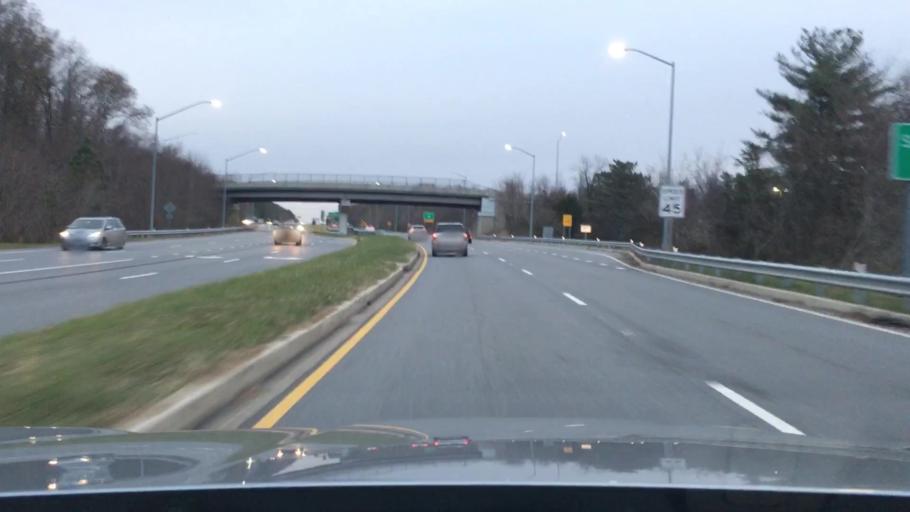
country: US
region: Maryland
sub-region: Prince George's County
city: Laurel
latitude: 39.1193
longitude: -76.8525
